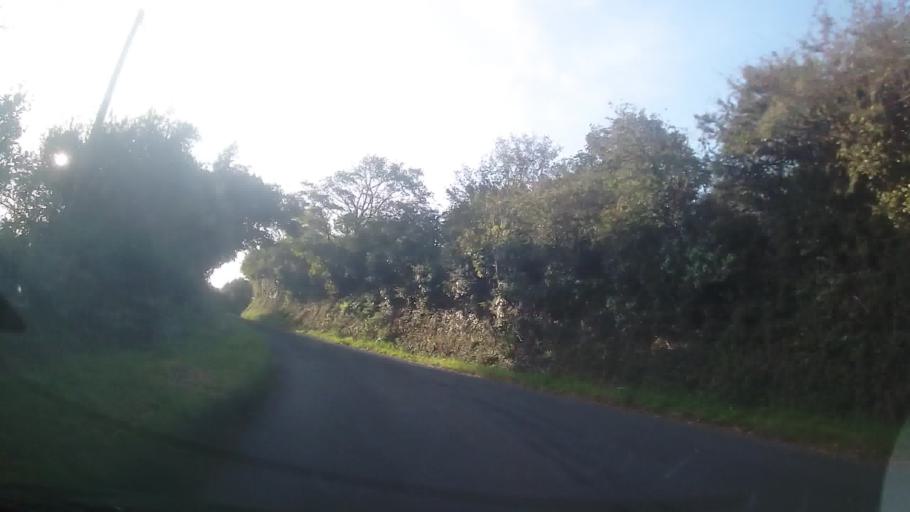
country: GB
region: Wales
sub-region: Pembrokeshire
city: Fishguard
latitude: 51.9840
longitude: -4.9539
